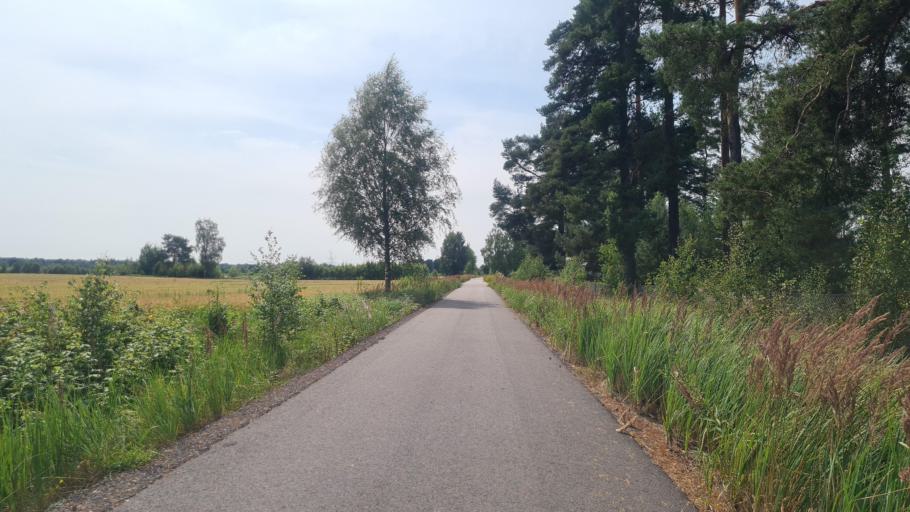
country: SE
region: Kronoberg
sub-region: Ljungby Kommun
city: Lagan
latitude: 56.9015
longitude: 13.9896
